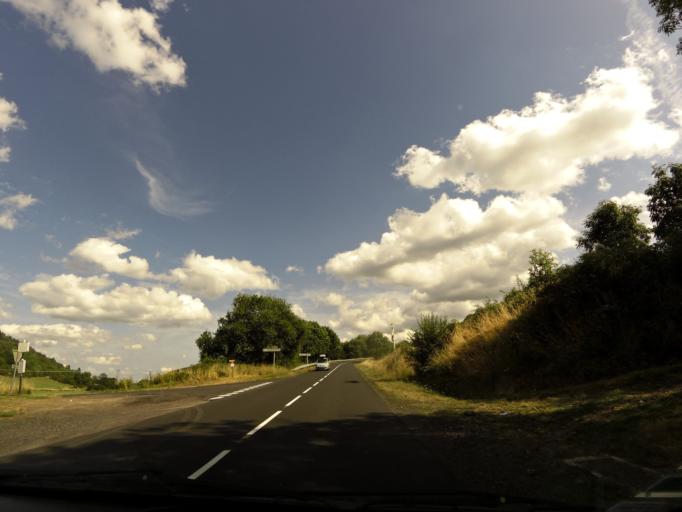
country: FR
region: Auvergne
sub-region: Departement du Puy-de-Dome
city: Aydat
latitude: 45.5584
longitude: 2.9475
